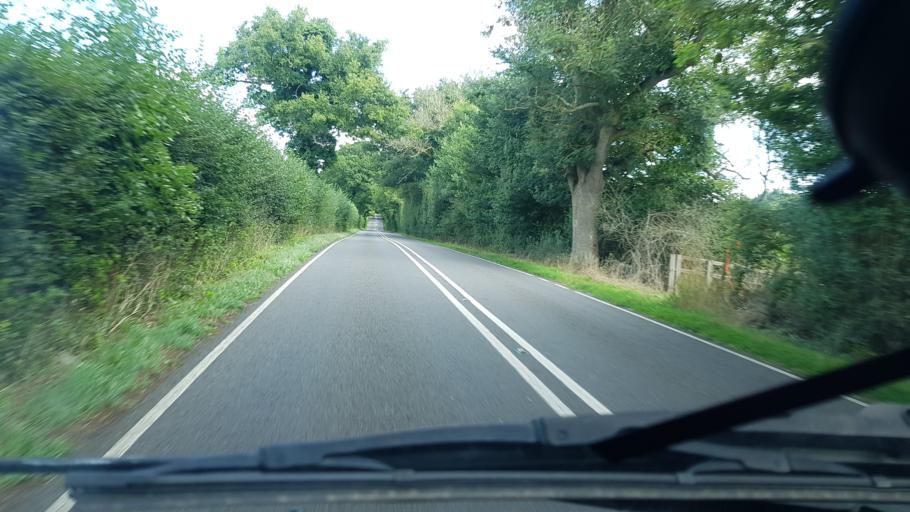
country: GB
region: England
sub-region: Surrey
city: Ockley
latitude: 51.0979
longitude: -0.3805
